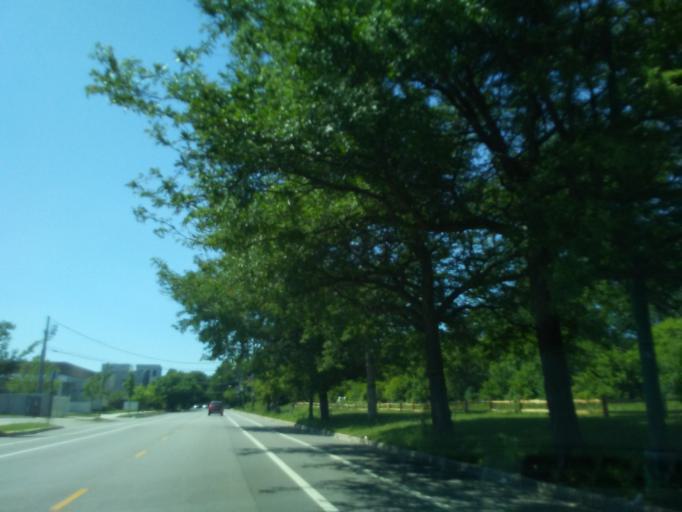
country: US
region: Illinois
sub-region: Cook County
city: Lincolnwood
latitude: 42.0031
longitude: -87.7094
